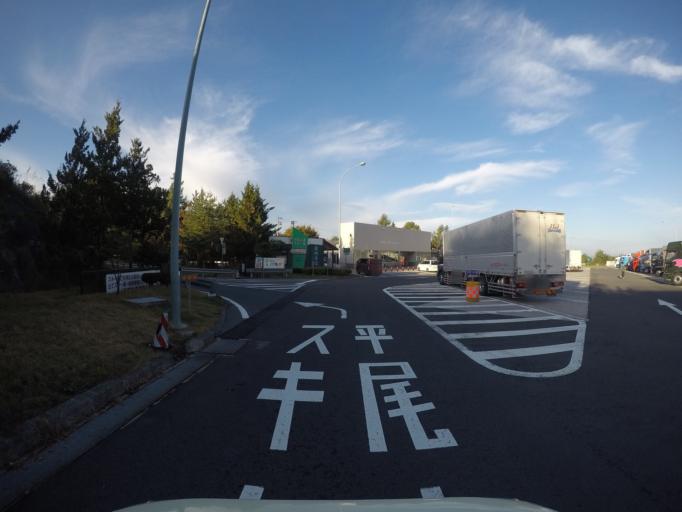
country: JP
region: Nagano
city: Saku
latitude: 36.2762
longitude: 138.5120
